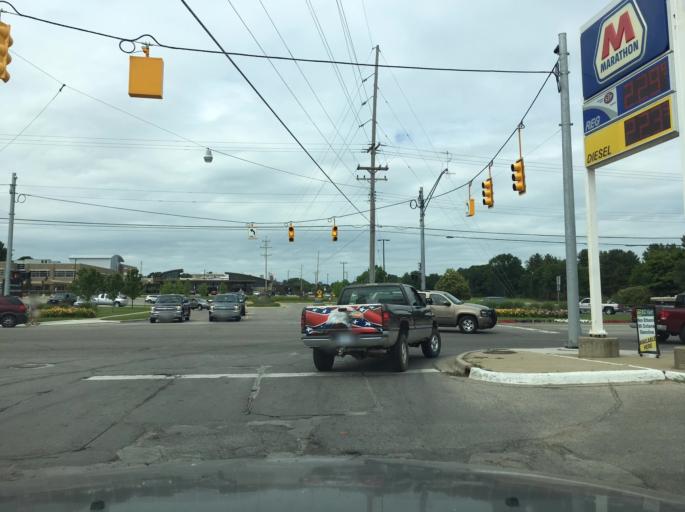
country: US
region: Michigan
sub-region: Mason County
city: Ludington
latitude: 43.9558
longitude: -86.4293
